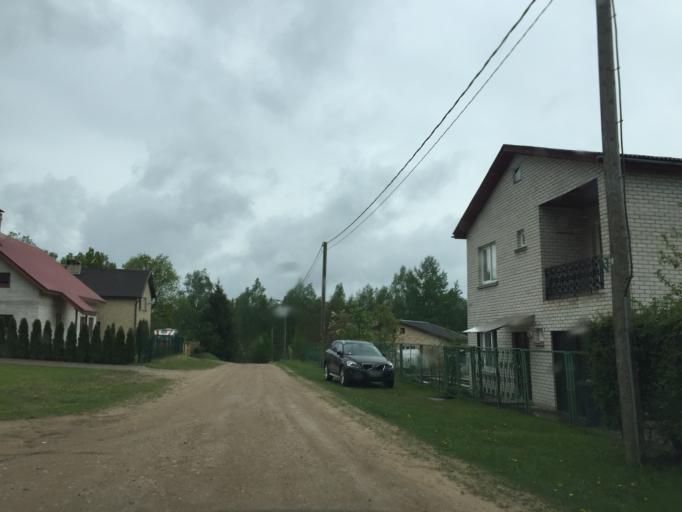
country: LV
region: Kegums
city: Kegums
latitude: 56.7435
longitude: 24.7266
